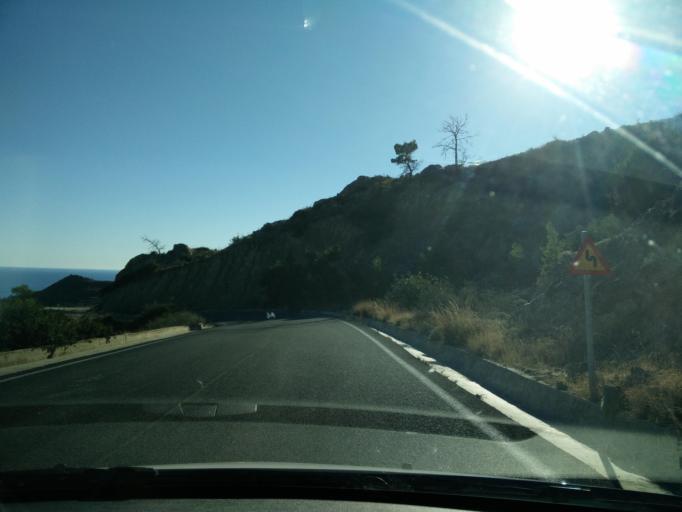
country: GR
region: Crete
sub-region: Nomos Lasithiou
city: Gra Liyia
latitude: 35.0178
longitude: 25.5787
